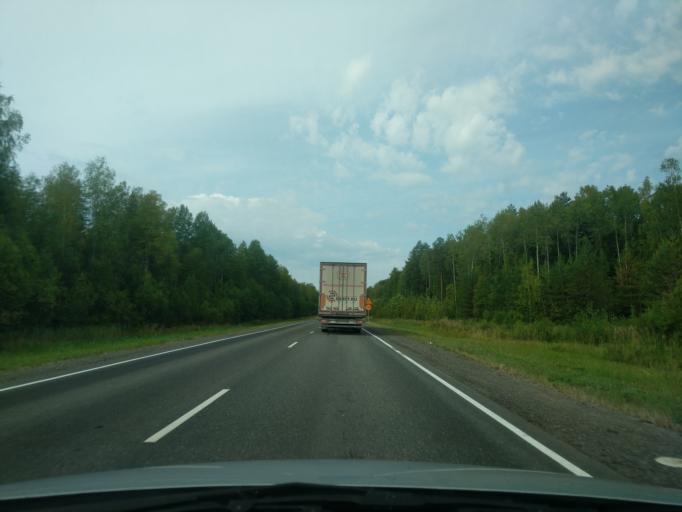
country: RU
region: Kirov
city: Leninskoye
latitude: 58.3191
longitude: 46.8583
